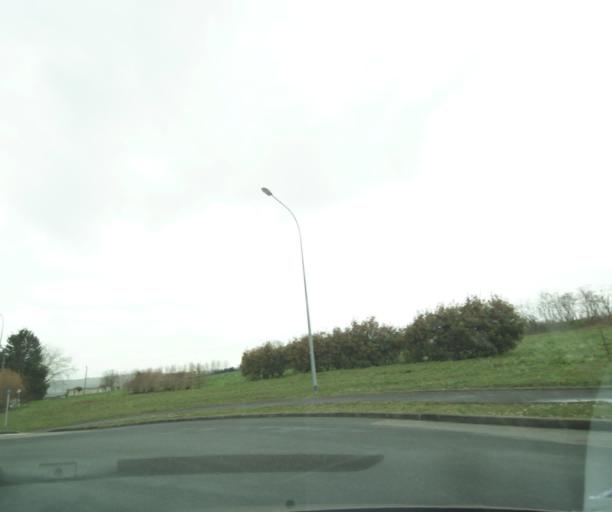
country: FR
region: Picardie
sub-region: Departement de l'Oise
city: Noyon
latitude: 49.5894
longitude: 3.0025
